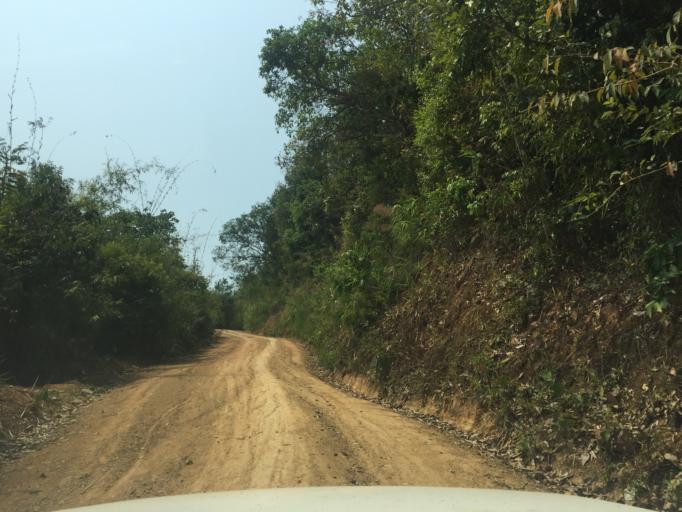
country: LA
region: Loungnamtha
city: Muang Nale
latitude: 20.6303
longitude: 101.6398
